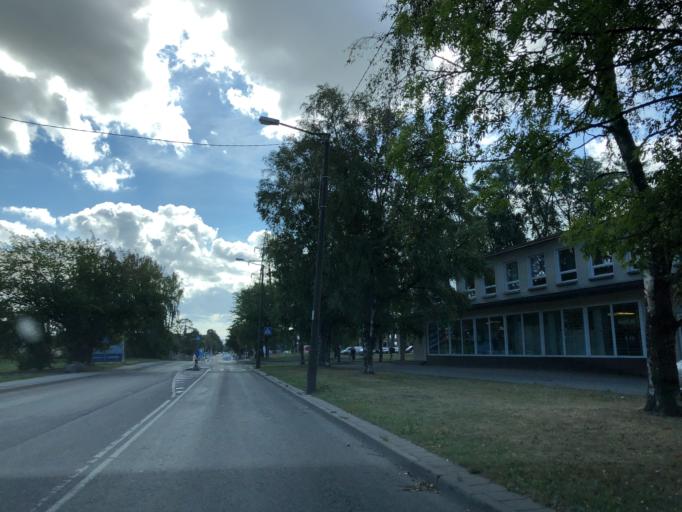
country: EE
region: Harju
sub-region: Tallinna linn
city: Tallinn
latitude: 59.4532
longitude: 24.7163
